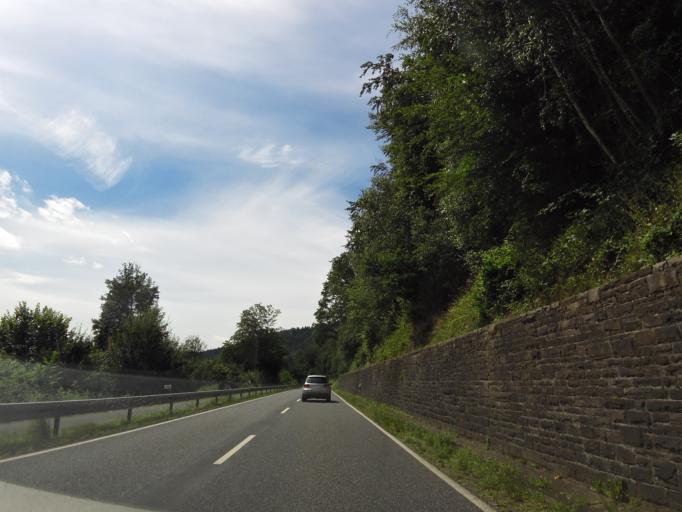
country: DE
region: Lower Saxony
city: Bad Karlshafen
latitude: 51.6456
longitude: 9.4928
